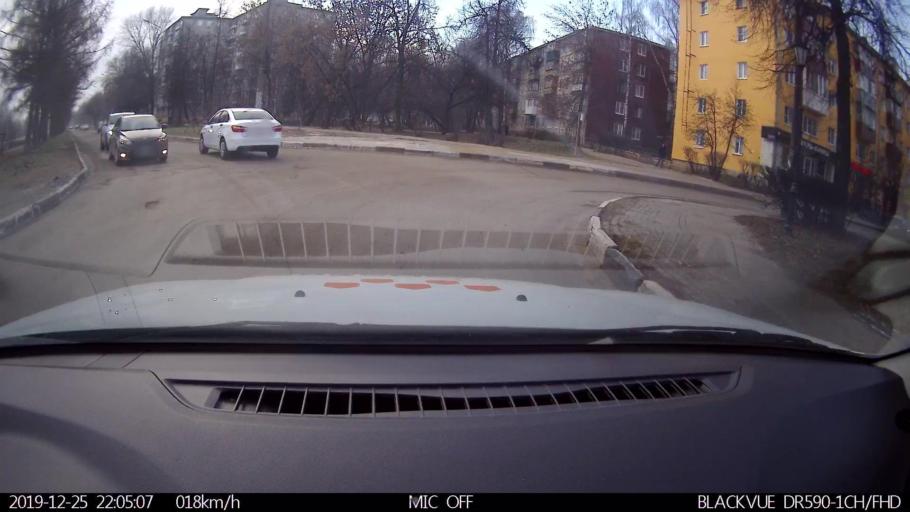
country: RU
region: Nizjnij Novgorod
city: Neklyudovo
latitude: 56.3447
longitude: 43.8727
